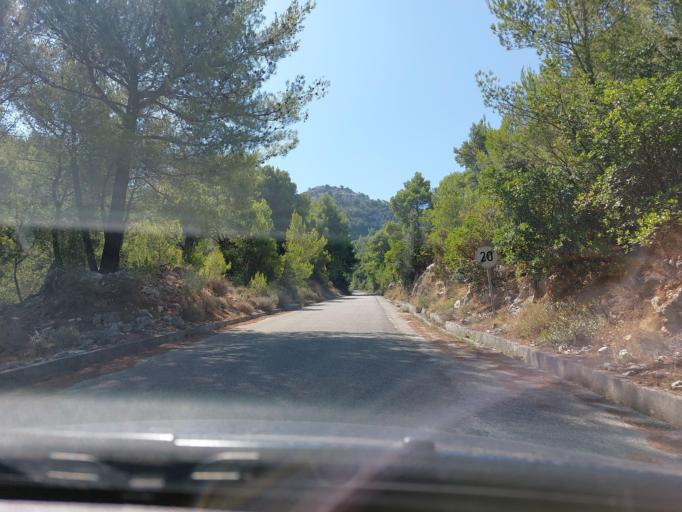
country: HR
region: Dubrovacko-Neretvanska
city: Smokvica
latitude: 42.7471
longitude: 16.8460
